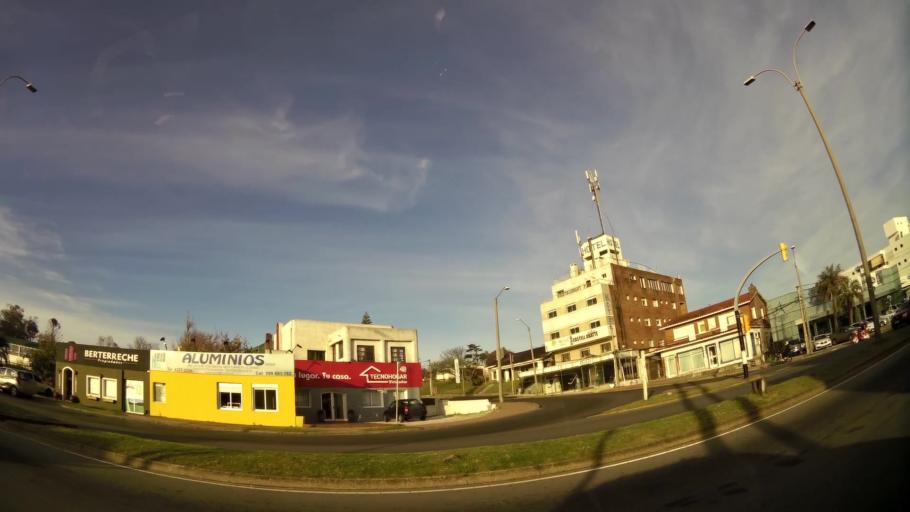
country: UY
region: Maldonado
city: Maldonado
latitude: -34.9193
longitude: -54.9719
